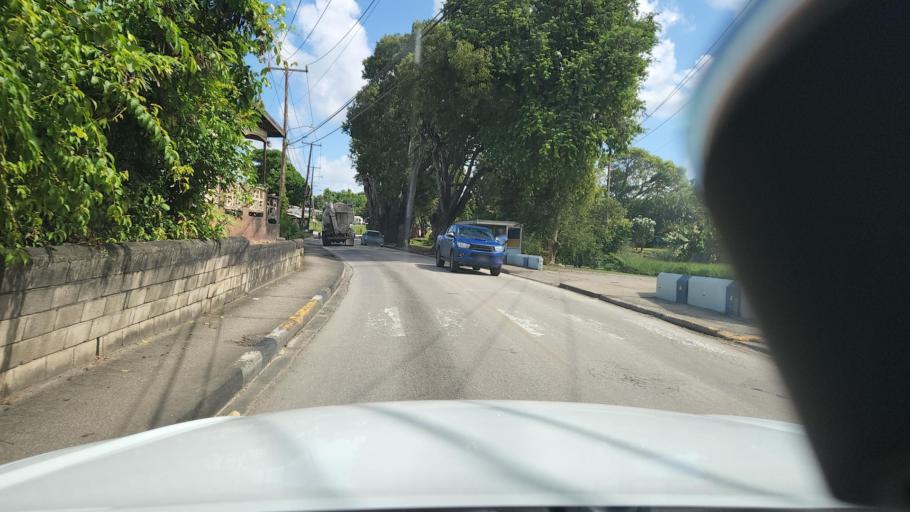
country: BB
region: Saint Thomas
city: Welchman Hall
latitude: 13.1312
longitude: -59.5652
